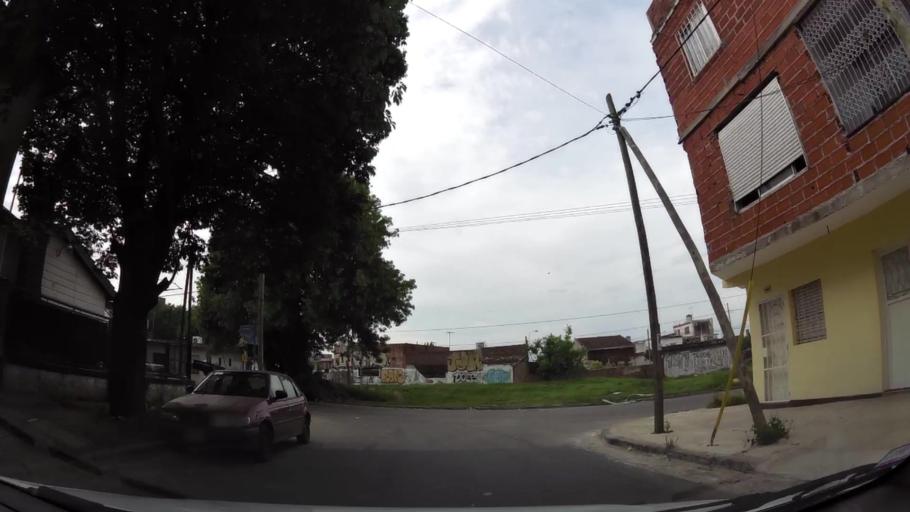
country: AR
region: Buenos Aires F.D.
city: Villa Lugano
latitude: -34.6846
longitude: -58.4951
